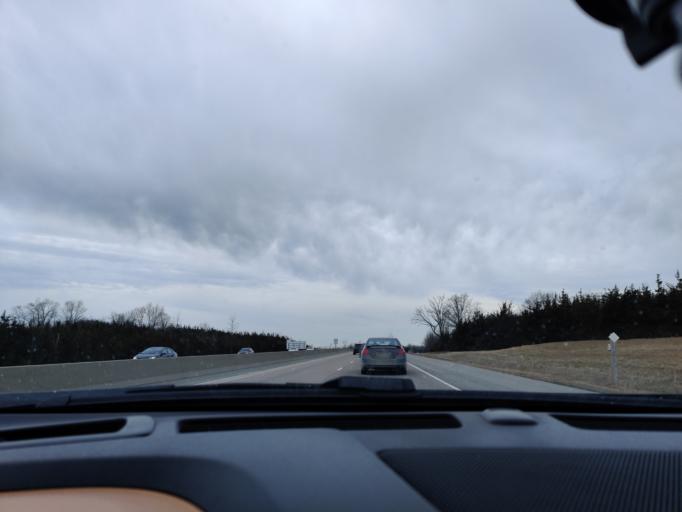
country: CA
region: Ontario
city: Belleville
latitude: 44.2179
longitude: -77.2562
